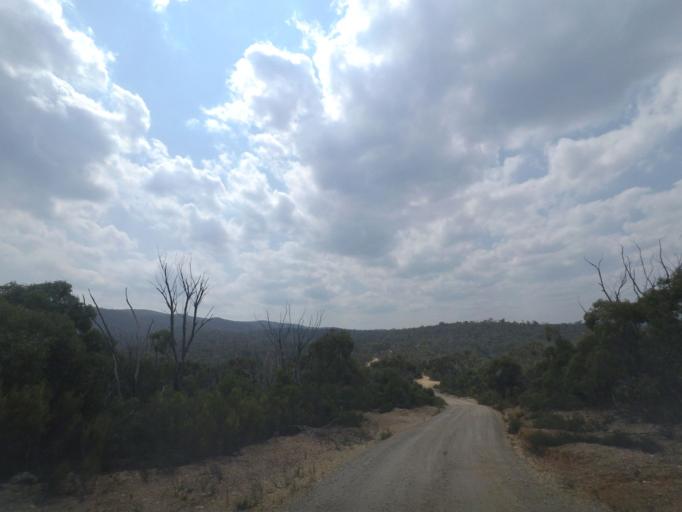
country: AU
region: Victoria
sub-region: Moorabool
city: Bacchus Marsh
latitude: -37.5753
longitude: 144.4383
